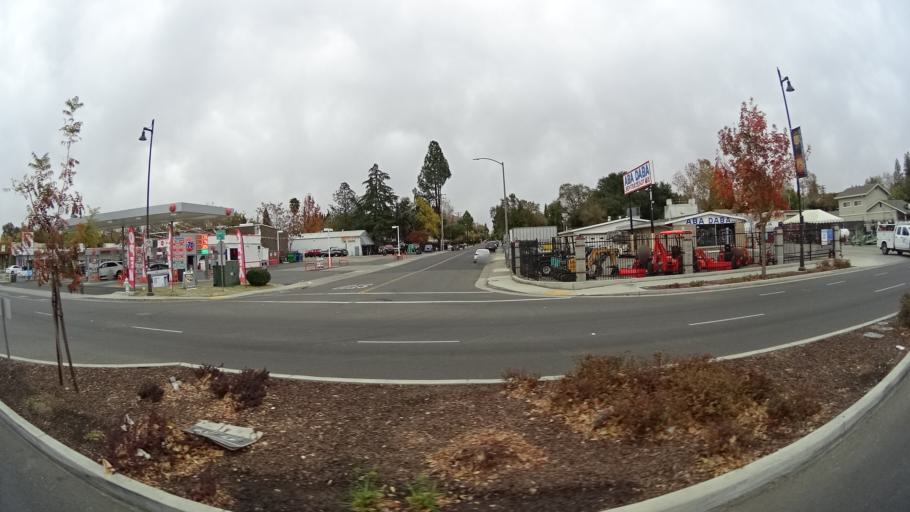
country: US
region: California
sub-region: Sacramento County
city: Citrus Heights
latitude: 38.7020
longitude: -121.2903
